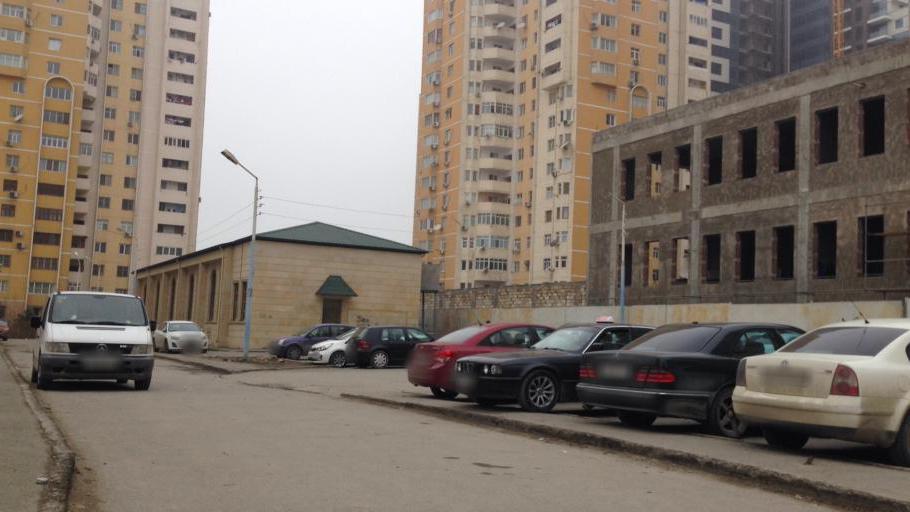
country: AZ
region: Baki
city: Baku
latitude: 40.3872
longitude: 49.8692
